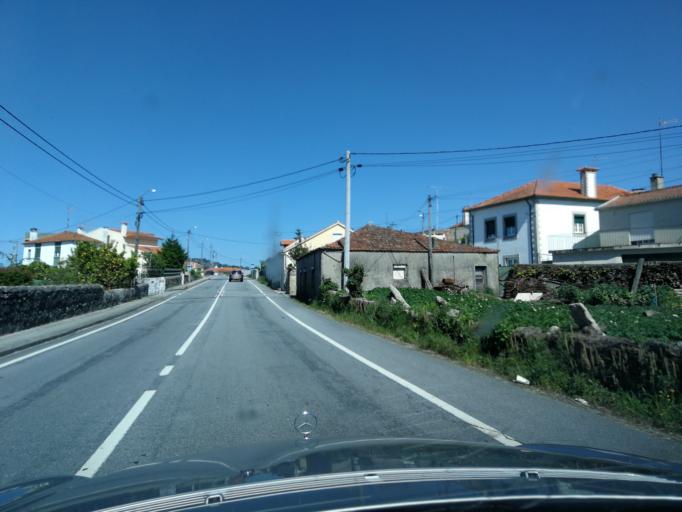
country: PT
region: Viana do Castelo
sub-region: Viana do Castelo
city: Meadela
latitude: 41.7061
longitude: -8.7880
